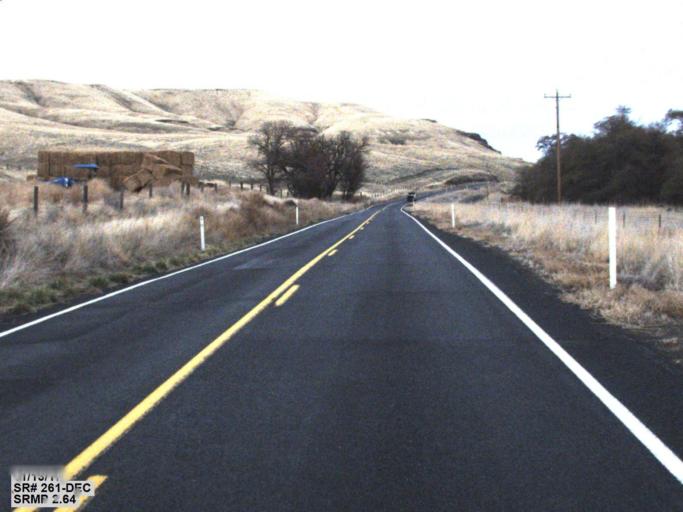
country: US
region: Washington
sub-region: Columbia County
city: Dayton
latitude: 46.5045
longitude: -118.0215
